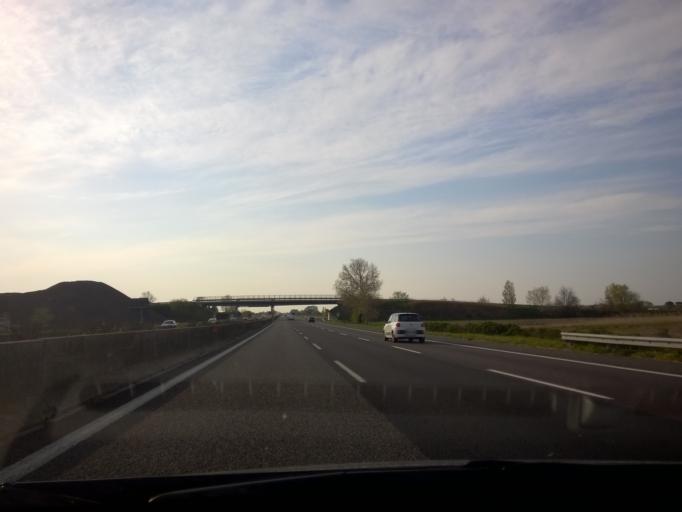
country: IT
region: Emilia-Romagna
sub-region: Forli-Cesena
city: Santa Maria Nuova
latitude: 44.2008
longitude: 12.2111
